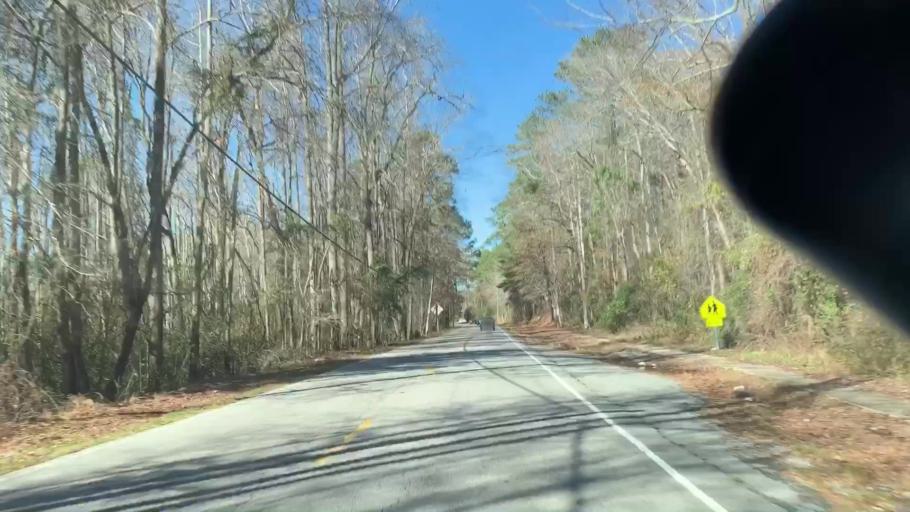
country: US
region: South Carolina
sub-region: Richland County
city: Woodfield
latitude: 34.0793
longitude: -80.9216
